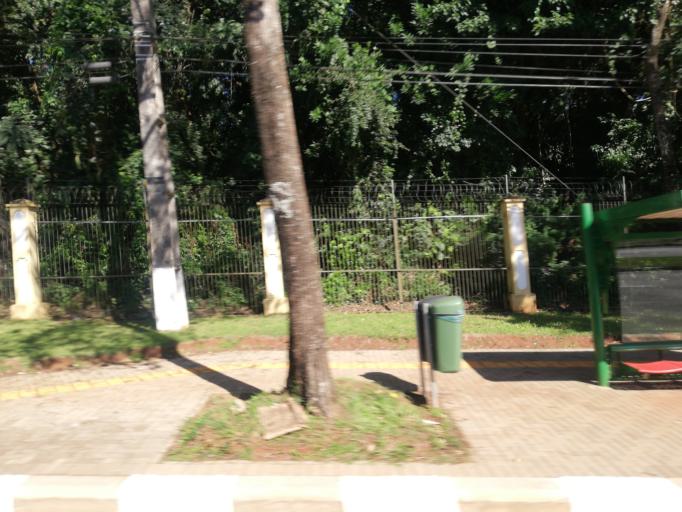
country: BR
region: Parana
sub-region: Foz Do Iguacu
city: Foz do Iguacu
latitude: -25.5573
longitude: -54.5640
